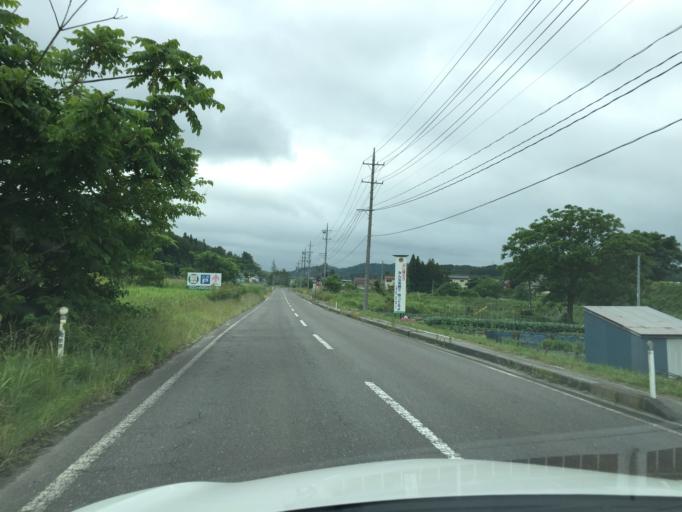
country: JP
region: Fukushima
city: Funehikimachi-funehiki
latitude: 37.4163
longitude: 140.6078
